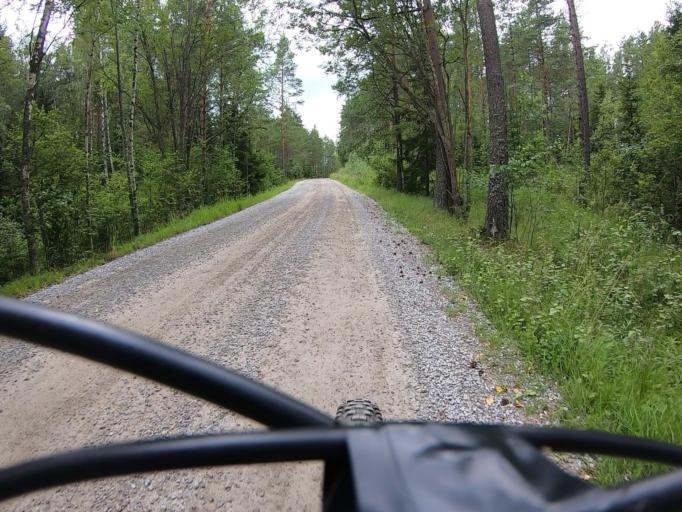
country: FI
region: Varsinais-Suomi
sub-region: Vakka-Suomi
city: Uusikaupunki
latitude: 60.8453
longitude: 21.3903
